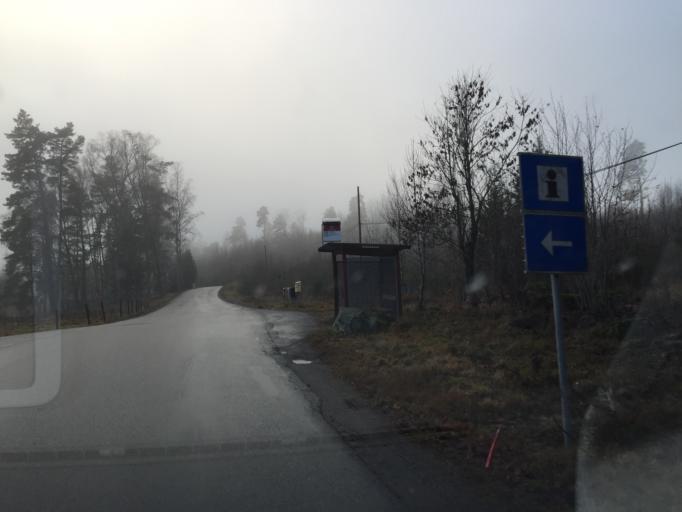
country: SE
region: Stockholm
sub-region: Nynashamns Kommun
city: Osmo
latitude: 59.0854
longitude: 17.9017
